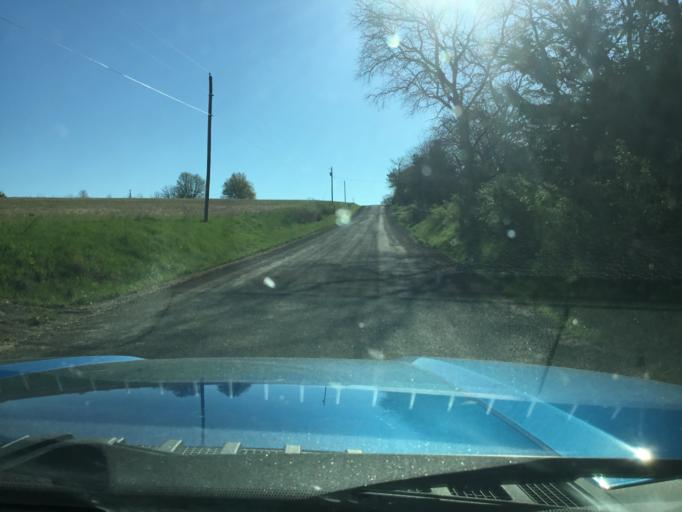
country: US
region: Kansas
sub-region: Douglas County
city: Lawrence
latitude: 38.9569
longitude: -95.3490
